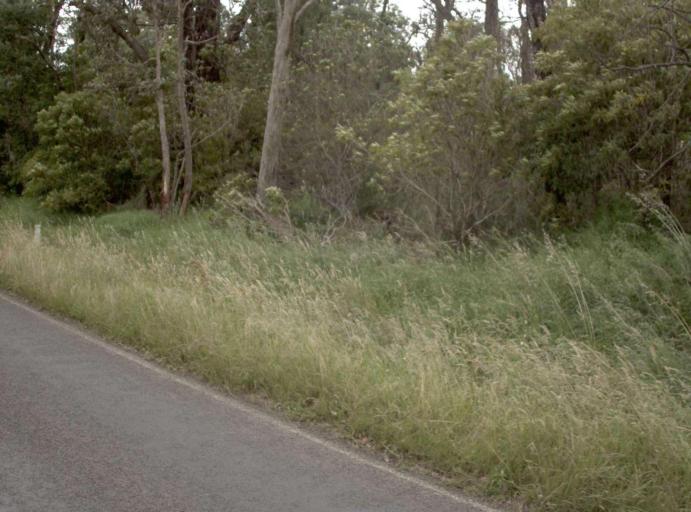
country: AU
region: Victoria
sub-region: Baw Baw
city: Warragul
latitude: -38.0909
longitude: 145.8514
